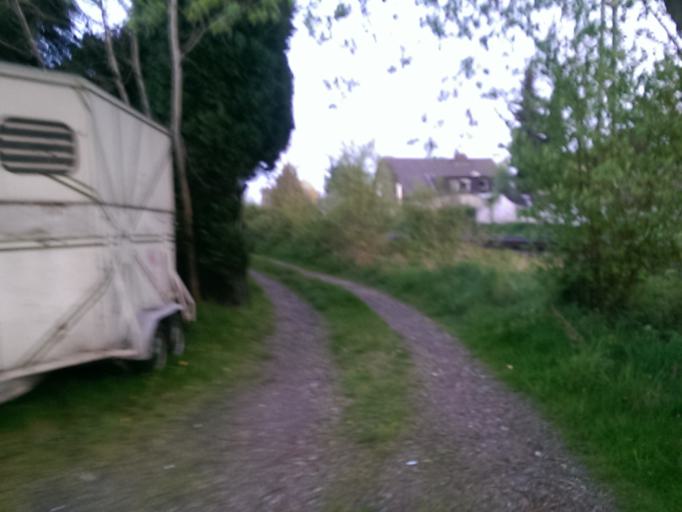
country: DE
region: North Rhine-Westphalia
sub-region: Regierungsbezirk Munster
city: Muenster
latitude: 51.9204
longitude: 7.6339
